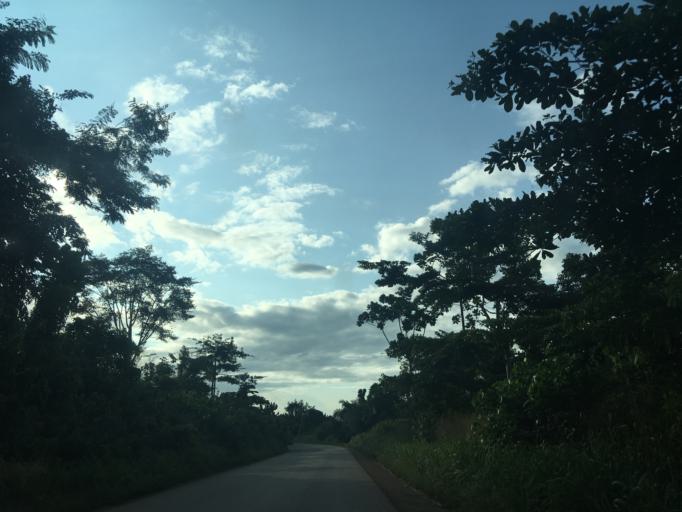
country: GH
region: Western
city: Bibiani
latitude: 6.2825
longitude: -2.2266
